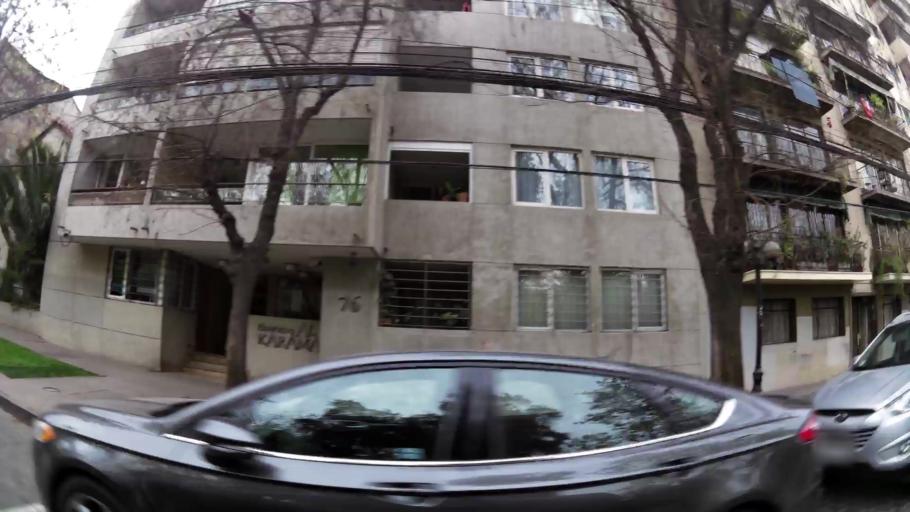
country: CL
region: Santiago Metropolitan
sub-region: Provincia de Santiago
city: Santiago
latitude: -33.4401
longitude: -70.6316
